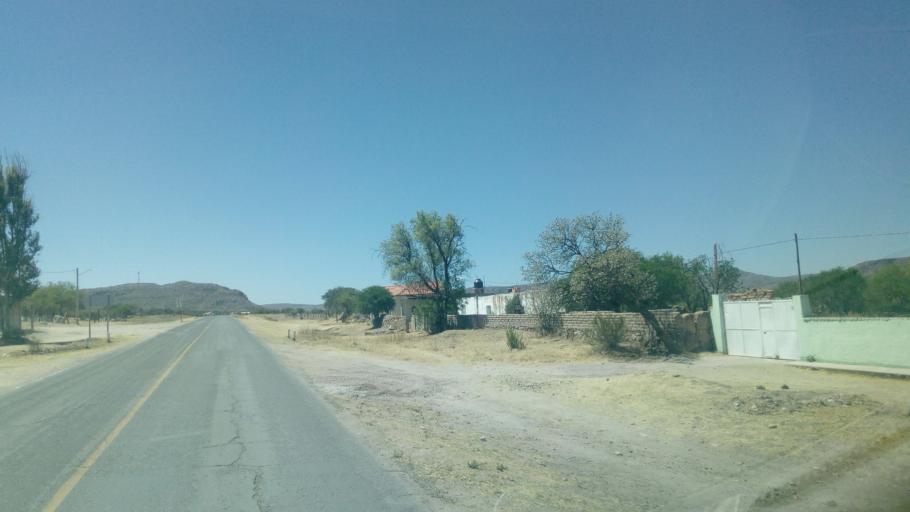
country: MX
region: Durango
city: Victoria de Durango
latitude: 24.1663
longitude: -104.7034
